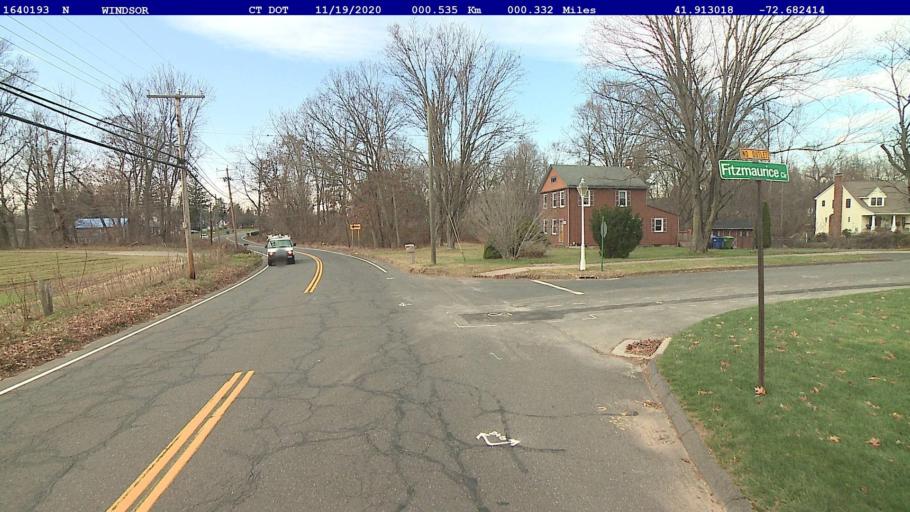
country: US
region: Connecticut
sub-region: Hartford County
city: Windsor Locks
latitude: 41.9130
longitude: -72.6824
